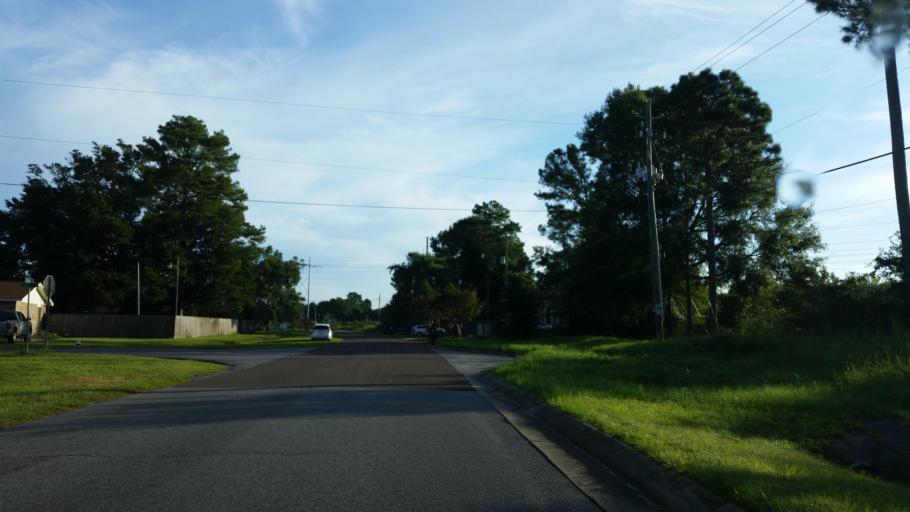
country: US
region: Florida
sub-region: Escambia County
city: Bellview
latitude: 30.4687
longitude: -87.2915
